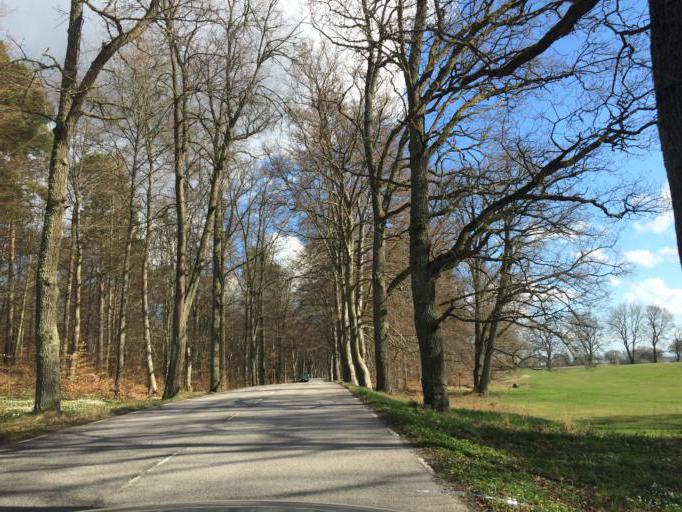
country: SE
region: Soedermanland
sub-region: Eskilstuna Kommun
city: Eskilstuna
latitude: 59.4436
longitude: 16.6237
